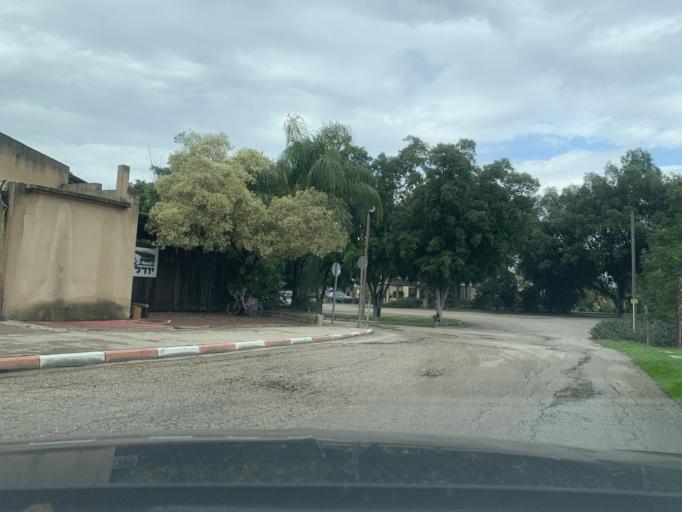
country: PS
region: West Bank
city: Qalqilyah
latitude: 32.2106
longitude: 34.9792
